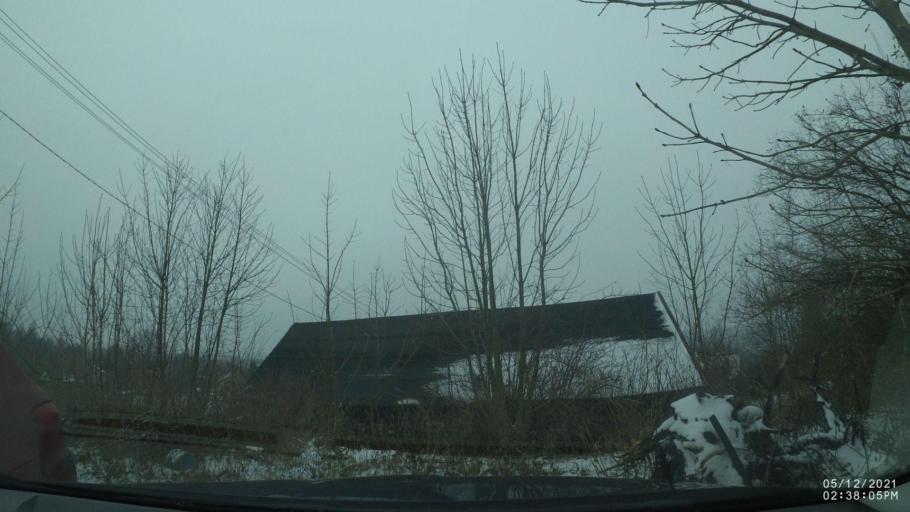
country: CZ
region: Kralovehradecky
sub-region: Okres Nachod
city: Nachod
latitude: 50.3933
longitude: 16.1740
